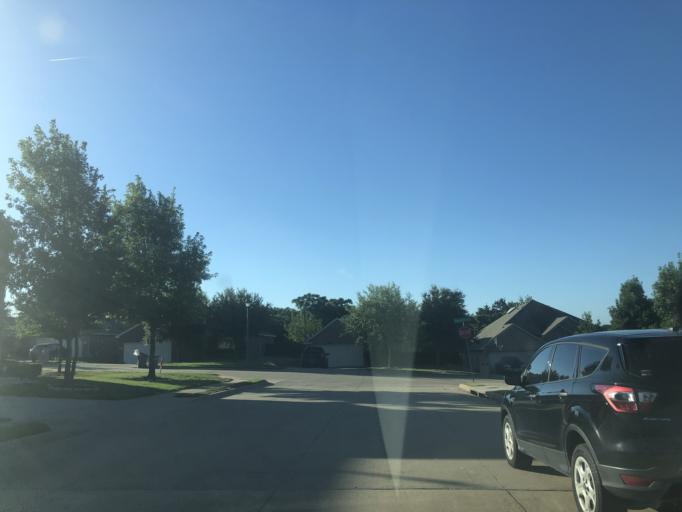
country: US
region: Texas
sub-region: Dallas County
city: Duncanville
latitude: 32.6579
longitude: -96.9496
